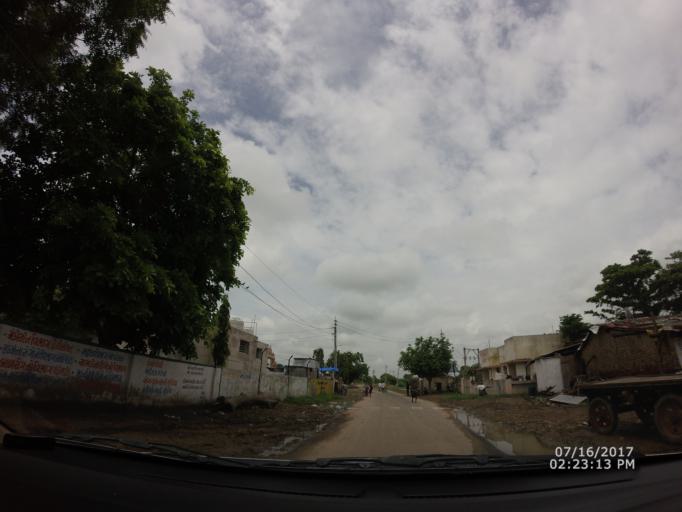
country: IN
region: Gujarat
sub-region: Ahmadabad
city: Sanand
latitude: 23.1328
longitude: 72.2977
